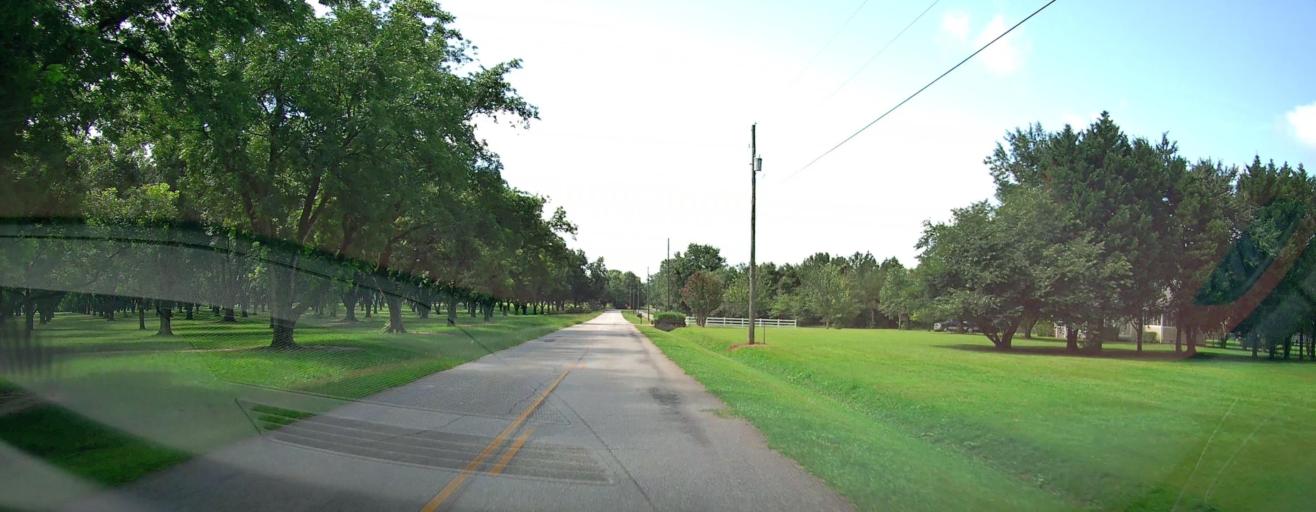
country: US
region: Georgia
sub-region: Peach County
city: Byron
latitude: 32.6549
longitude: -83.7814
